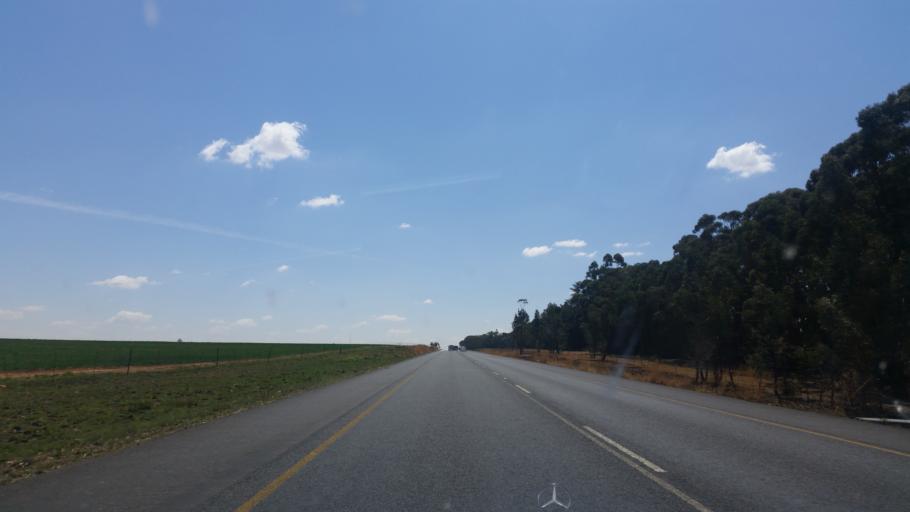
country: ZA
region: Orange Free State
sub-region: Thabo Mofutsanyana District Municipality
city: Bethlehem
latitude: -28.0986
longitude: 28.6573
